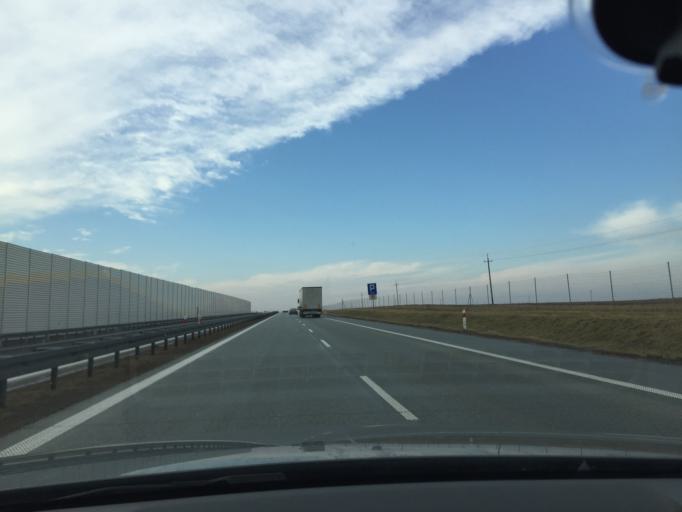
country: PL
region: Lodz Voivodeship
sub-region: Powiat skierniewicki
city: Kowiesy
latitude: 51.8525
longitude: 20.3710
